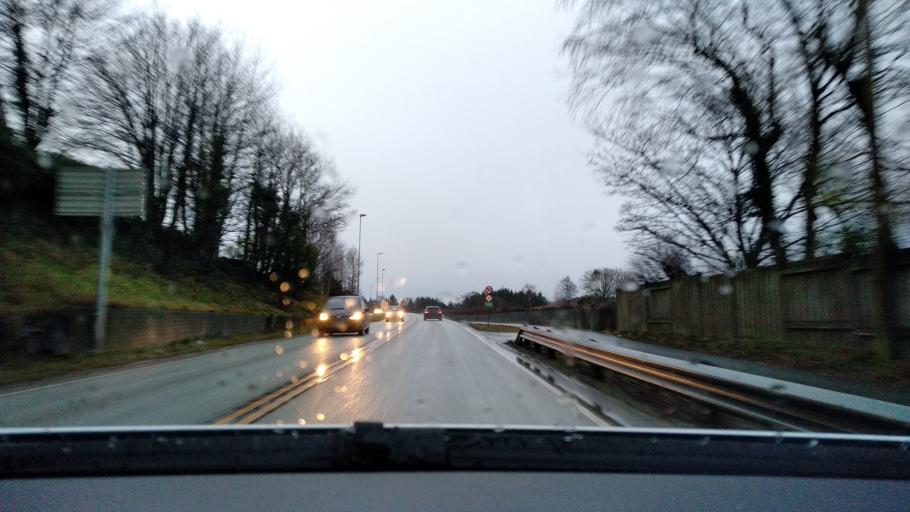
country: NO
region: Rogaland
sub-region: Randaberg
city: Randaberg
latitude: 58.9517
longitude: 5.6586
